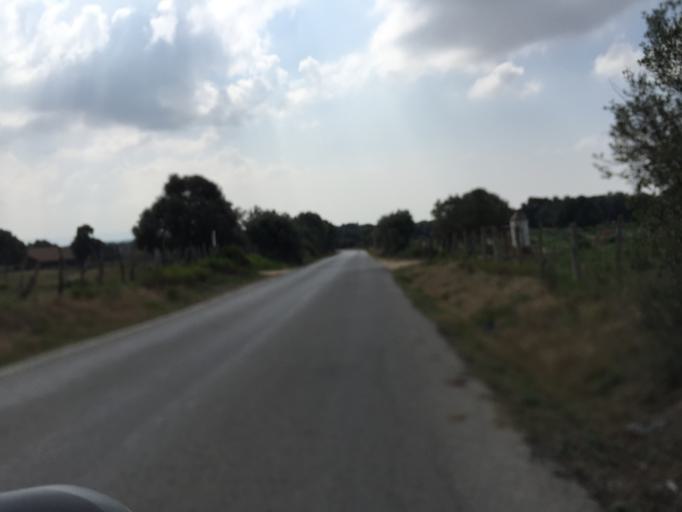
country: ES
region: Andalusia
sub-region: Provincia de Cadiz
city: Vejer de la Frontera
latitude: 36.2858
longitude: -5.9346
